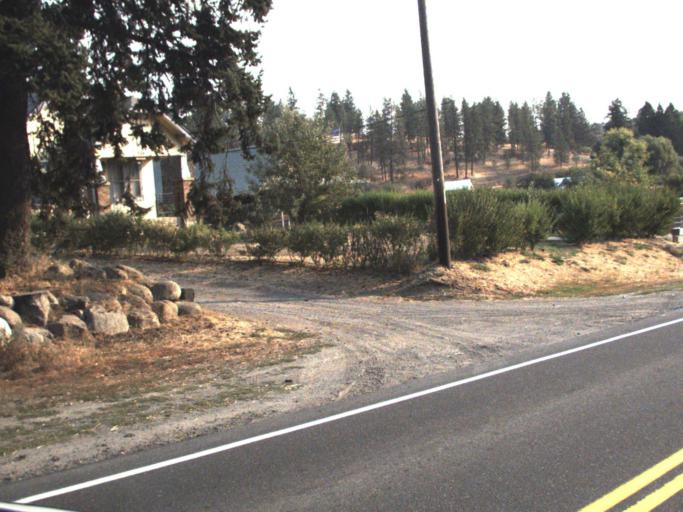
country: US
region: Washington
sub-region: Spokane County
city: Veradale
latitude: 47.4522
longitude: -117.1354
